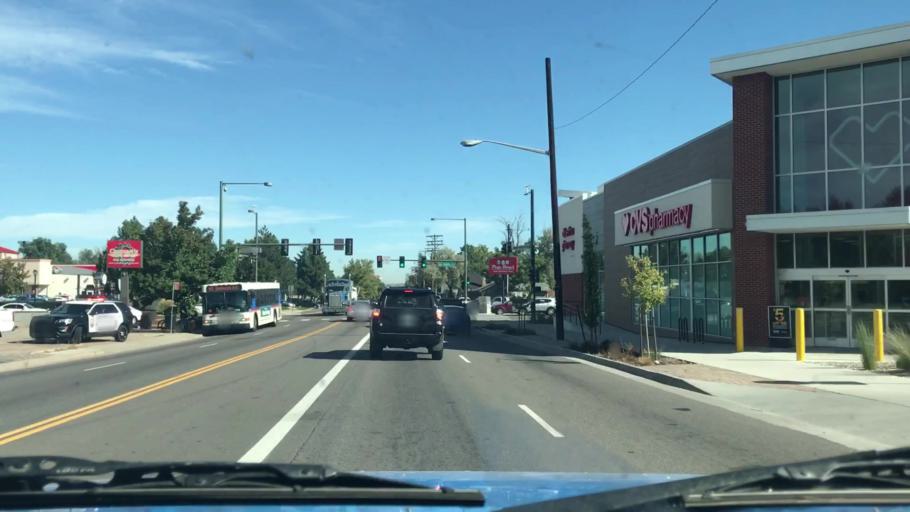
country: US
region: Colorado
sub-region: Jefferson County
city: Edgewater
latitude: 39.7686
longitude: -105.0532
